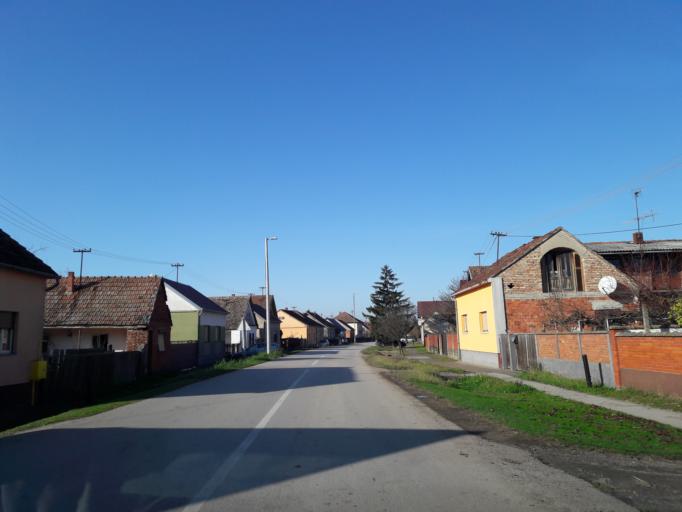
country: HR
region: Vukovarsko-Srijemska
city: Vodinci
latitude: 45.2699
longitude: 18.6130
